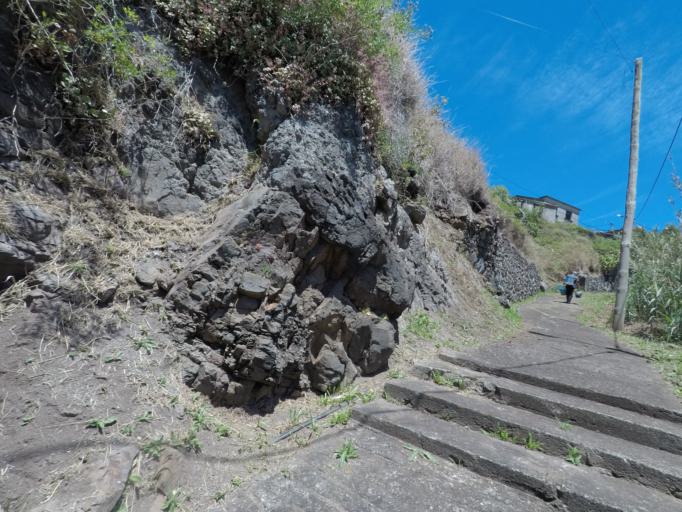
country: PT
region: Madeira
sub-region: Sao Vicente
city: Sao Vicente
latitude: 32.8243
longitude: -16.9788
